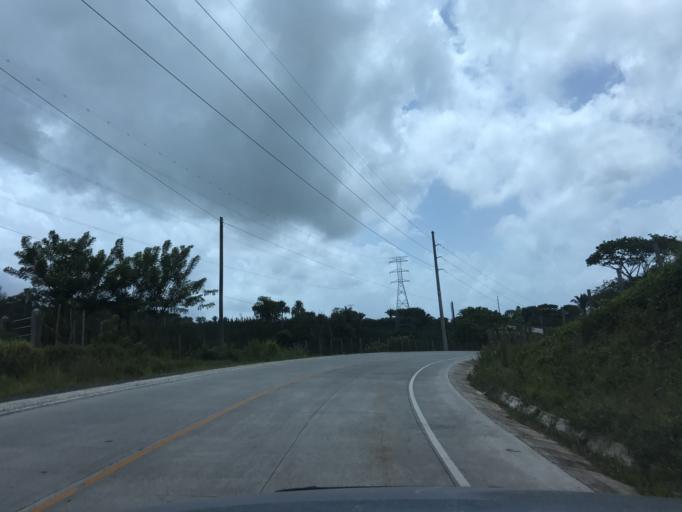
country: GT
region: Izabal
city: Morales
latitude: 15.6239
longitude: -89.0645
